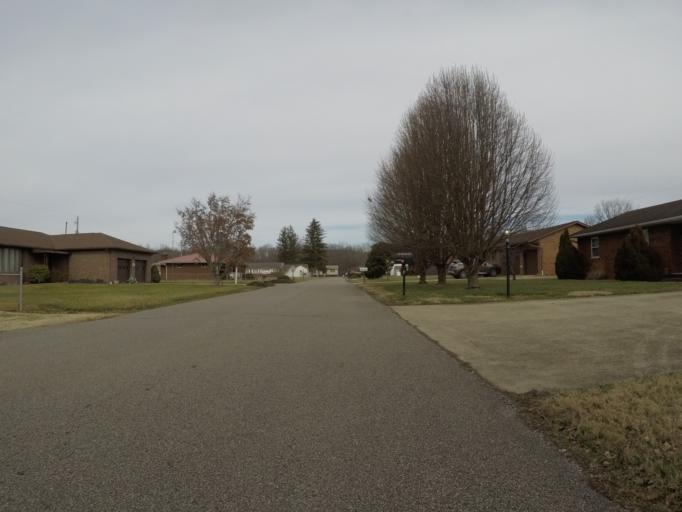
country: US
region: West Virginia
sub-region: Cabell County
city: Pea Ridge
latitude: 38.4525
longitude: -82.3463
